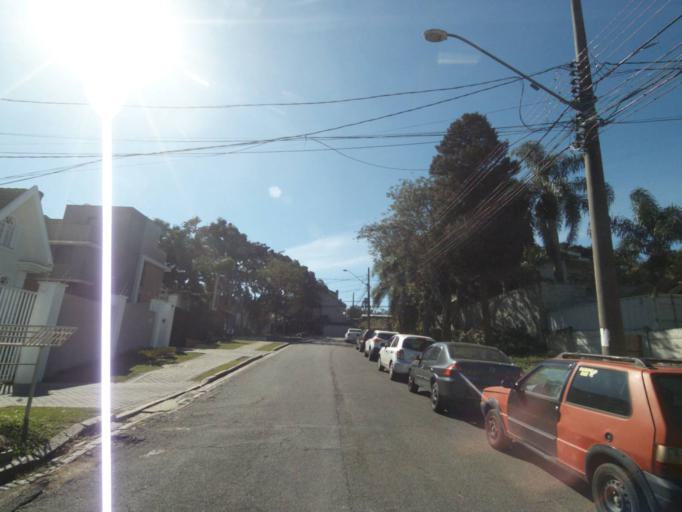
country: BR
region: Parana
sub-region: Curitiba
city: Curitiba
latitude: -25.4136
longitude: -49.2344
